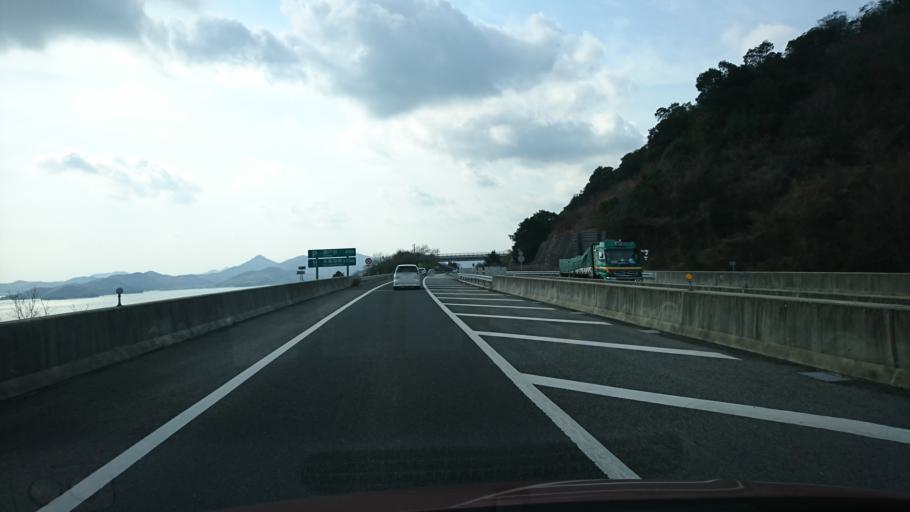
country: JP
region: Hiroshima
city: Innoshima
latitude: 34.2761
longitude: 133.1074
